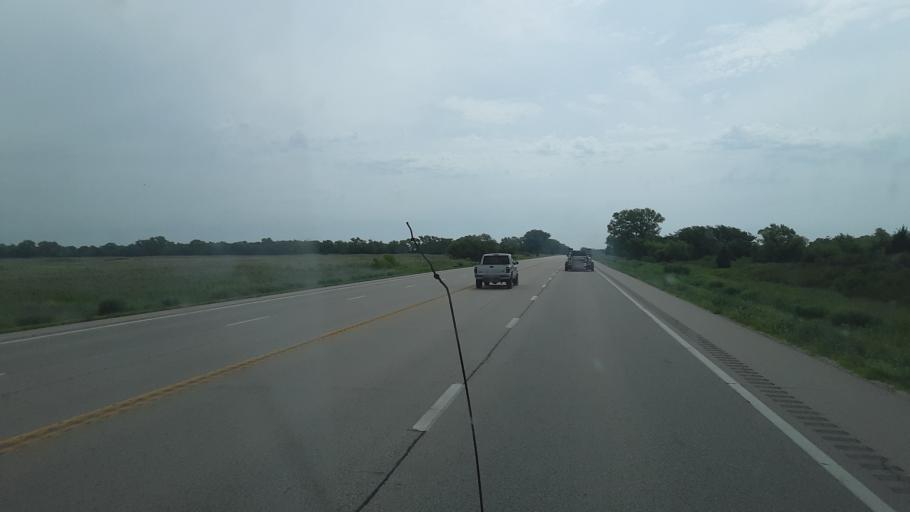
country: US
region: Kansas
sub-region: Rice County
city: Sterling
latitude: 37.9846
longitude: -98.2976
